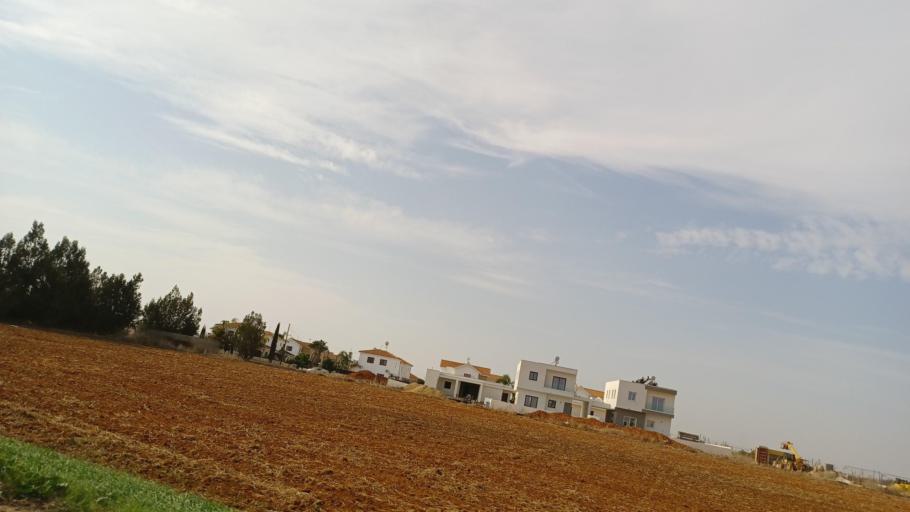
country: CY
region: Ammochostos
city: Frenaros
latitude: 35.0473
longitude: 33.9262
